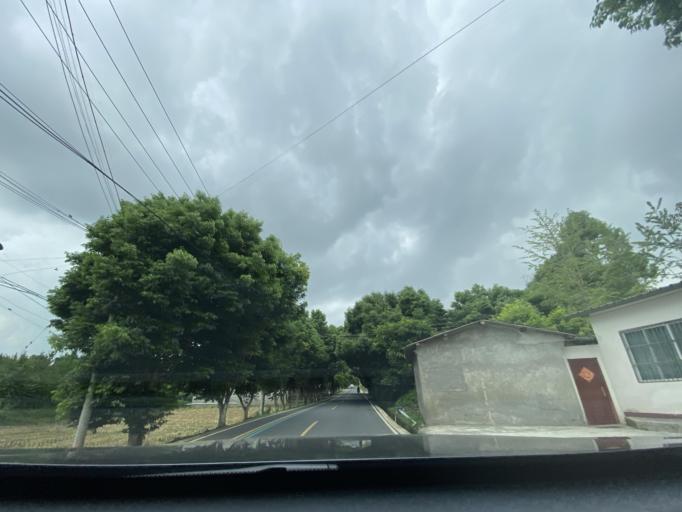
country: CN
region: Sichuan
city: Dongsheng
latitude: 30.4084
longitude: 103.9986
